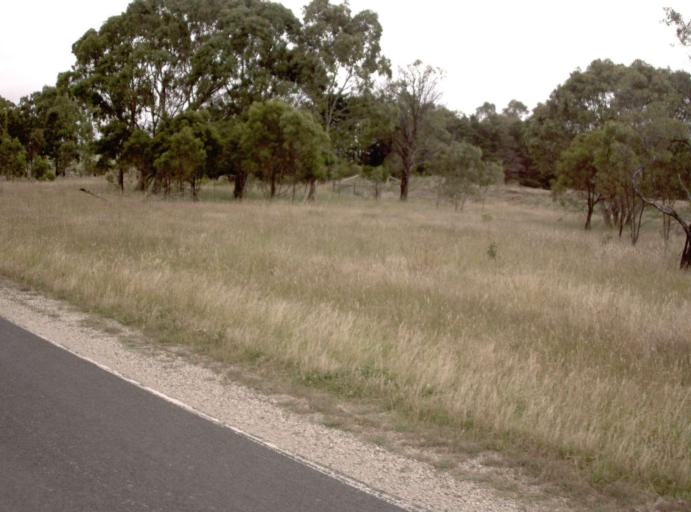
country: AU
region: Victoria
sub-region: Wellington
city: Heyfield
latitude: -38.0395
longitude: 146.7669
